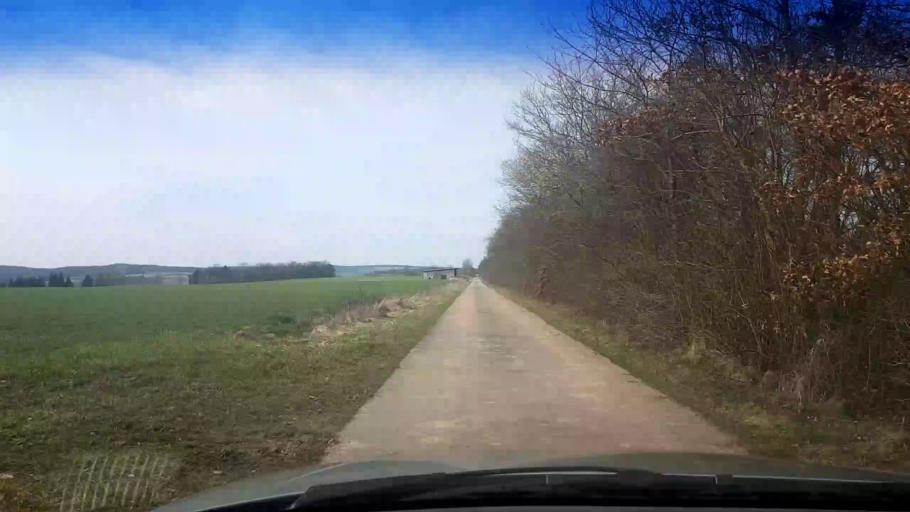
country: DE
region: Bavaria
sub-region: Upper Franconia
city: Burgebrach
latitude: 49.8168
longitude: 10.7569
